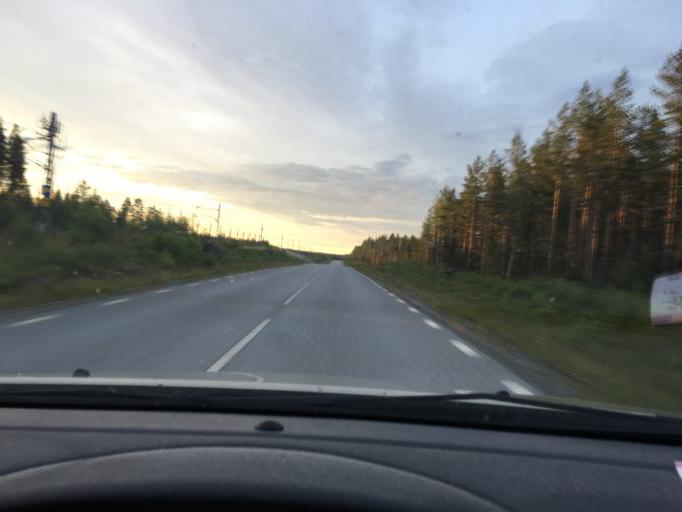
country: SE
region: Norrbotten
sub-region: Lulea Kommun
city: Ranea
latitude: 66.0414
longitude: 22.3374
